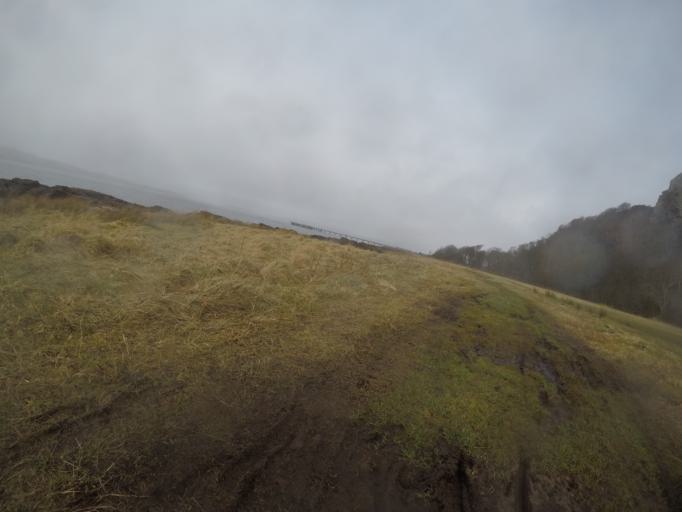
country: GB
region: Scotland
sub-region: North Ayrshire
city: Millport
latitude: 55.7111
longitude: -4.9037
